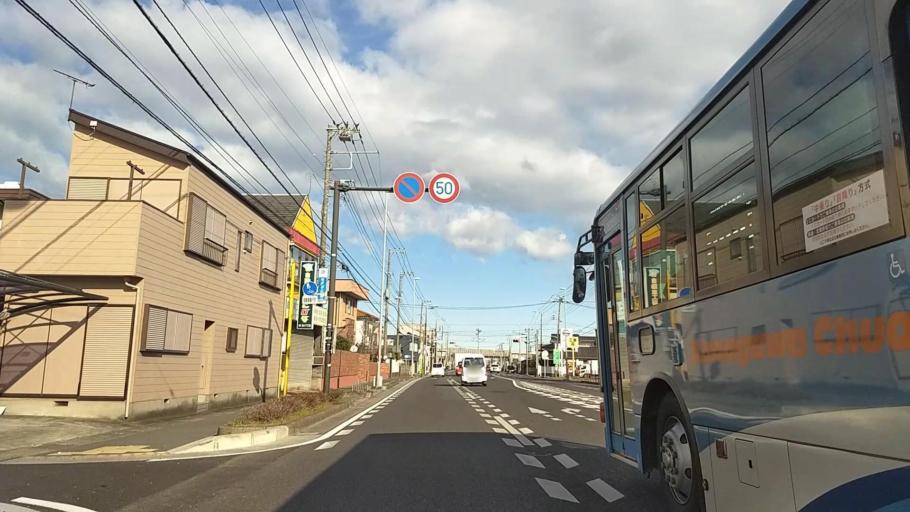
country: JP
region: Kanagawa
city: Isehara
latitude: 35.3827
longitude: 139.3616
